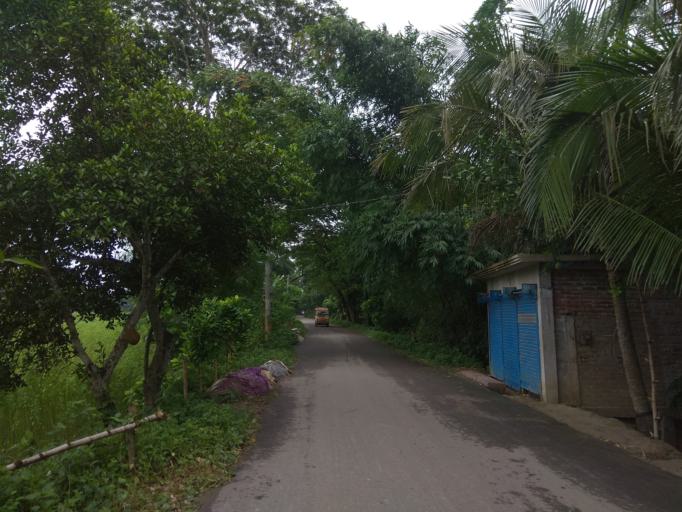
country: BD
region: Dhaka
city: Dohar
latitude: 23.4201
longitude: 90.0675
